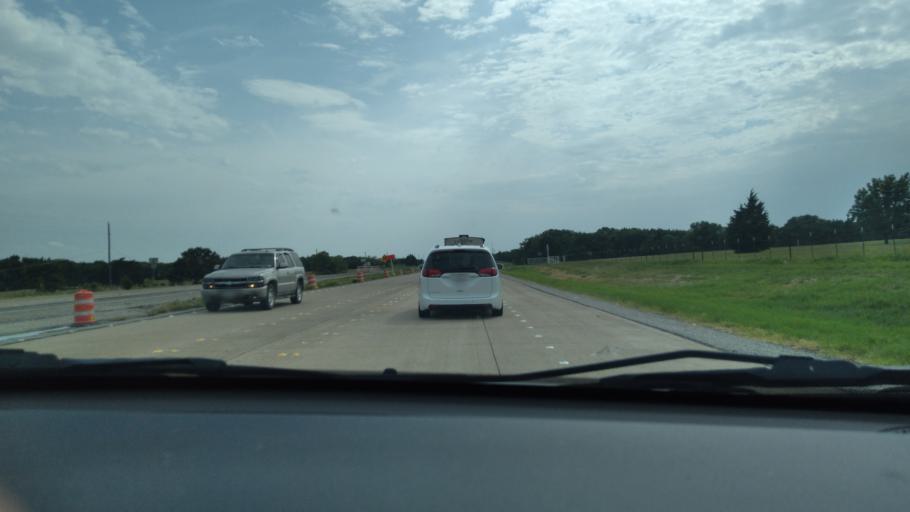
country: US
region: Texas
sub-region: Hill County
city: Hubbard
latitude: 31.8766
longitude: -96.7579
